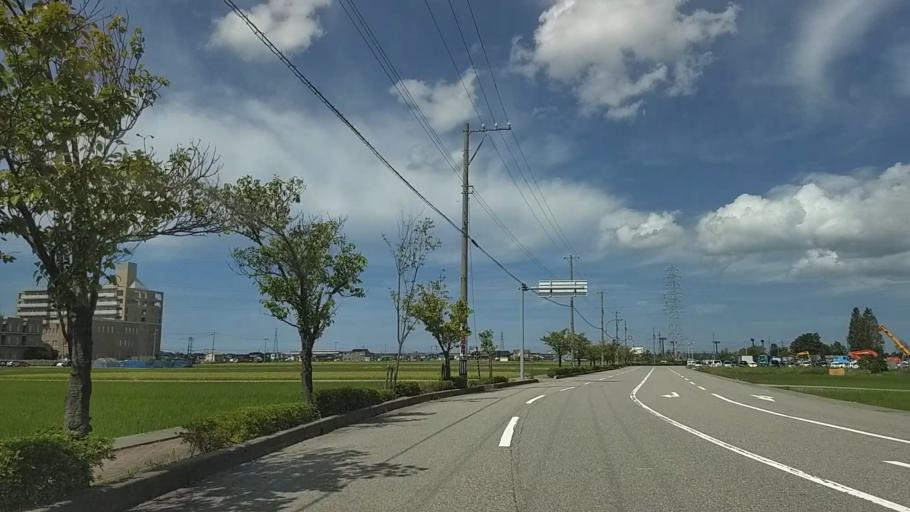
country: JP
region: Ishikawa
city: Kanazawa-shi
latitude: 36.5905
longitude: 136.6564
